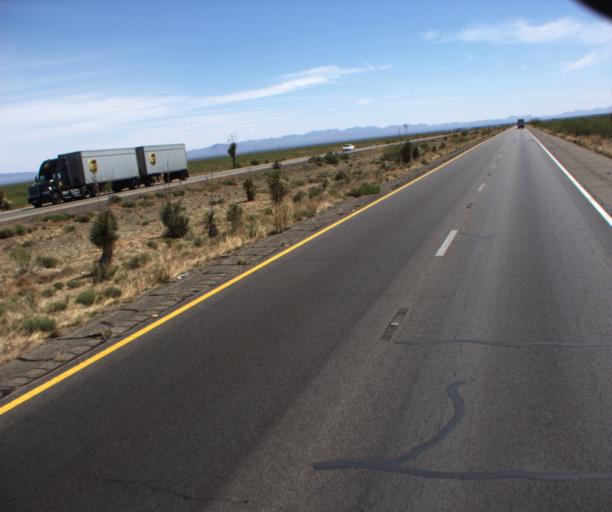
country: US
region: Arizona
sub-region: Cochise County
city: Willcox
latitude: 32.3396
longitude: -109.5589
